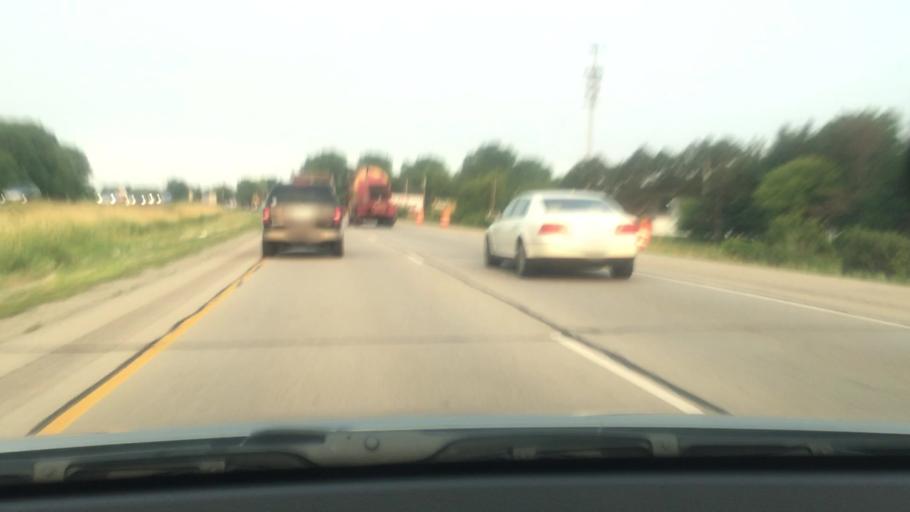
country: US
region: Wisconsin
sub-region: Outagamie County
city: Appleton
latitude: 44.2989
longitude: -88.4553
